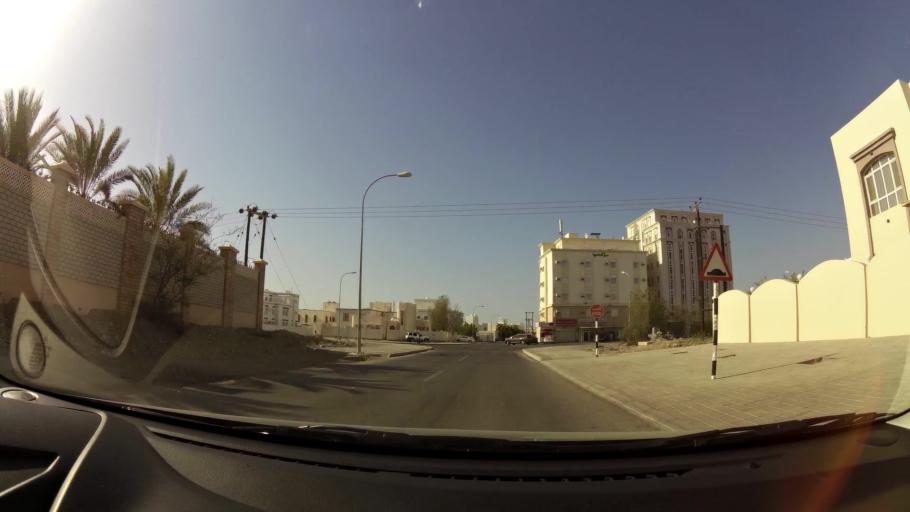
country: OM
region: Muhafazat Masqat
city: As Sib al Jadidah
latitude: 23.6208
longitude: 58.2005
